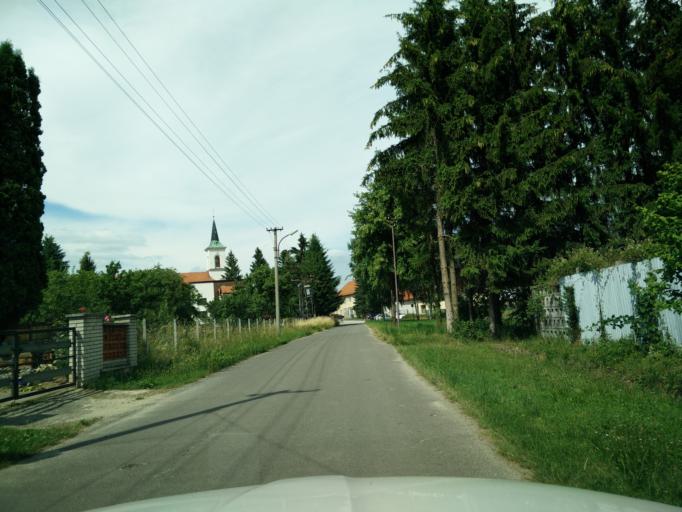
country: SK
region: Nitriansky
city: Prievidza
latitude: 48.8171
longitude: 18.6204
